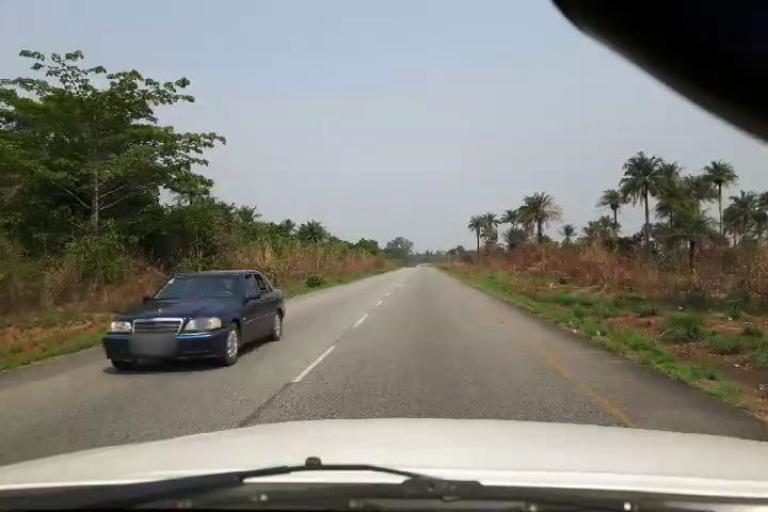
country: SL
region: Southern Province
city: Largo
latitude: 8.3079
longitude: -12.2082
